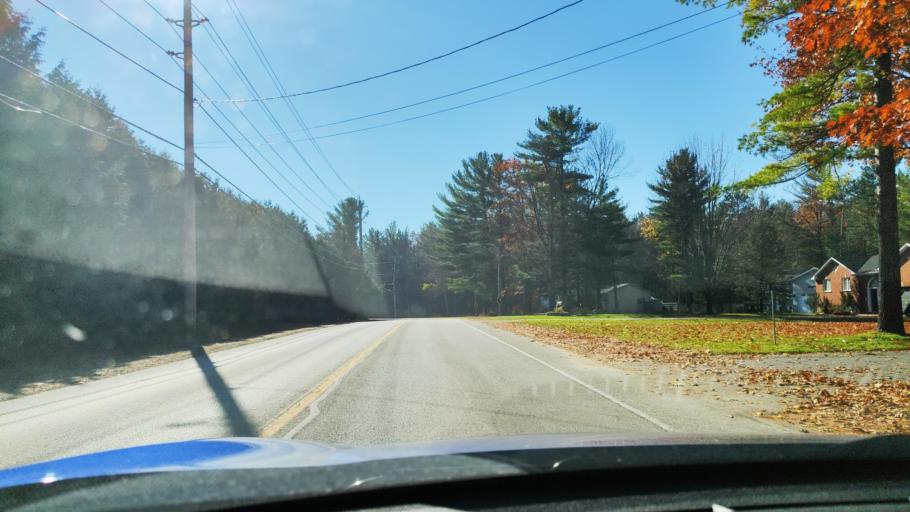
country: CA
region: Ontario
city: Wasaga Beach
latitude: 44.5115
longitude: -79.9962
